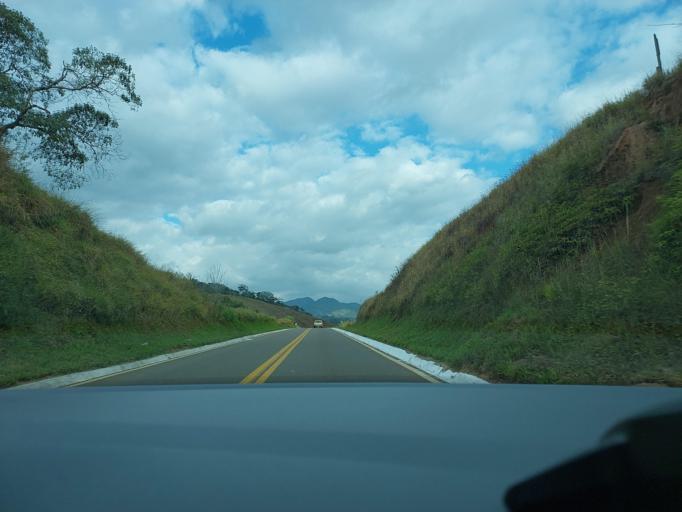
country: BR
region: Minas Gerais
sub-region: Visconde Do Rio Branco
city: Visconde do Rio Branco
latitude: -20.9231
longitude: -42.6374
